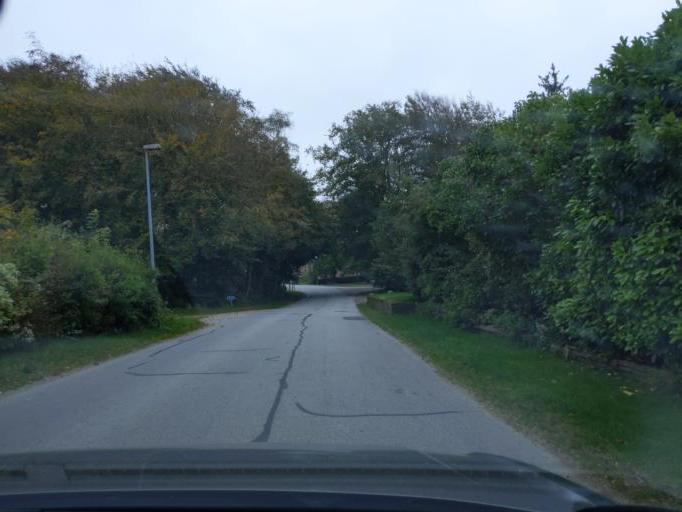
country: DK
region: Central Jutland
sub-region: Viborg Kommune
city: Viborg
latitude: 56.4828
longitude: 9.3035
